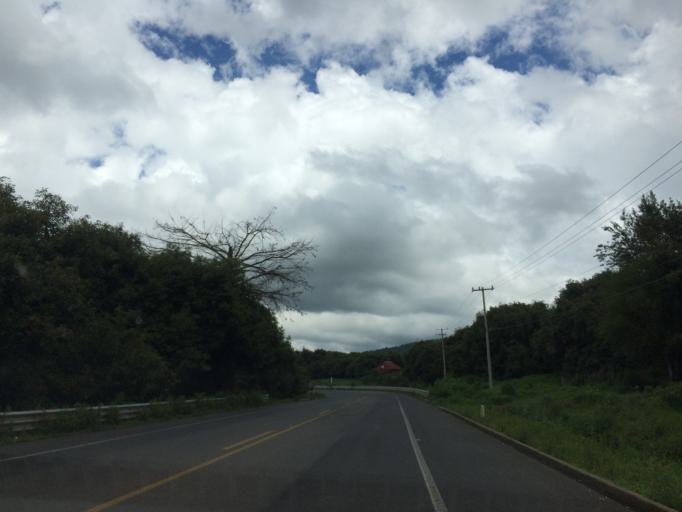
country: MX
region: Michoacan
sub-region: Uruapan
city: Santa Ana Zirosto
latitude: 19.5456
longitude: -102.3322
